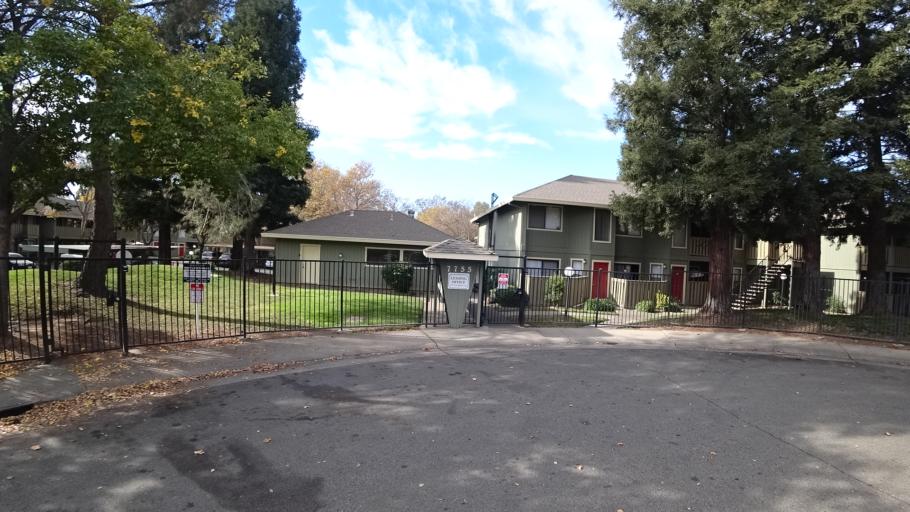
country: US
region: California
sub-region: Sacramento County
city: Citrus Heights
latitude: 38.6811
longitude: -121.2776
